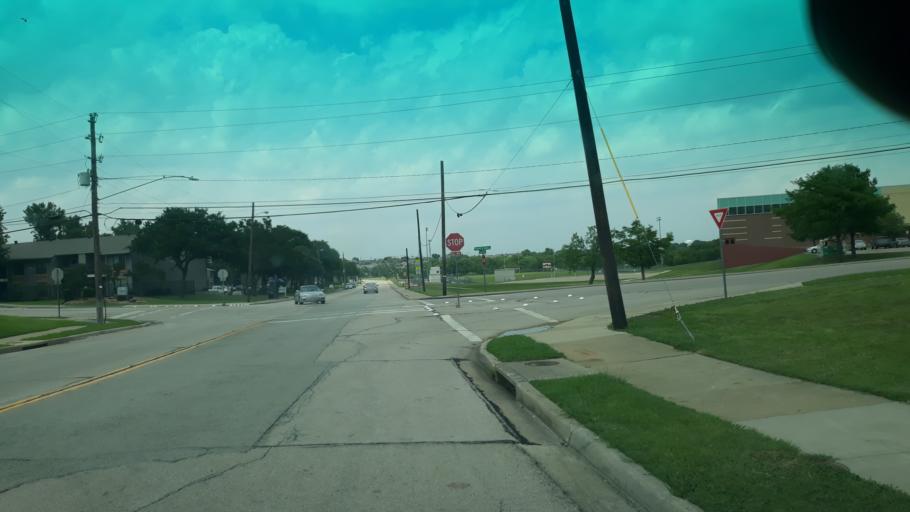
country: US
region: Texas
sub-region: Dallas County
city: Irving
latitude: 32.8599
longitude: -96.9885
